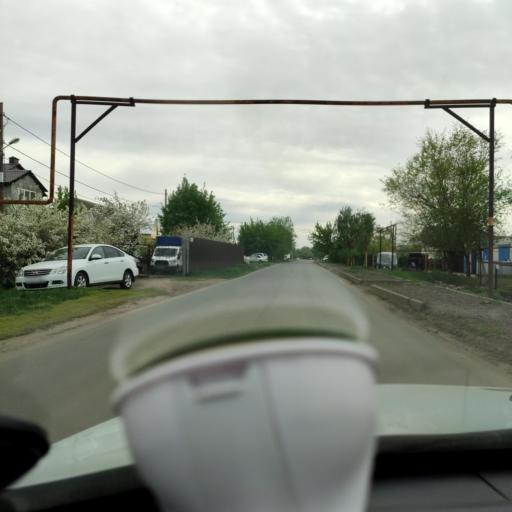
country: RU
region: Samara
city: Smyshlyayevka
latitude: 53.2210
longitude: 50.3369
